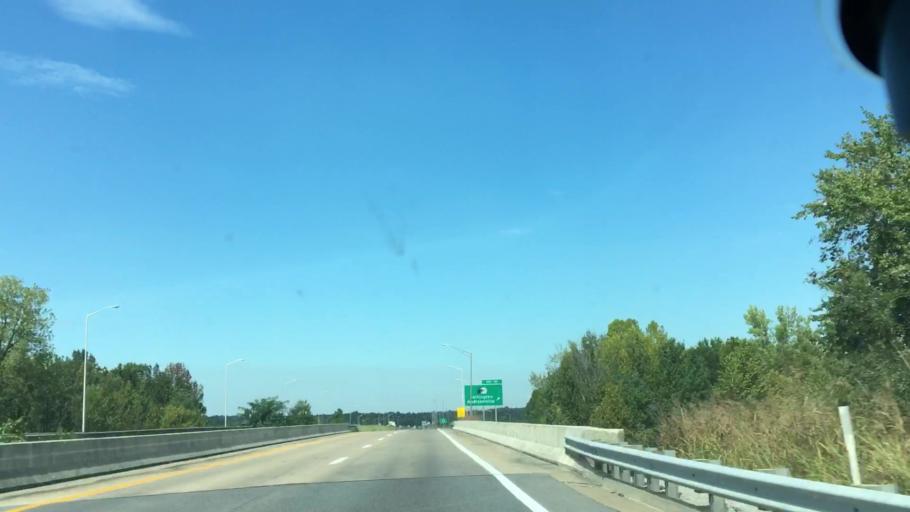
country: US
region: Kentucky
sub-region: Hopkins County
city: Madisonville
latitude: 37.2908
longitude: -87.4603
